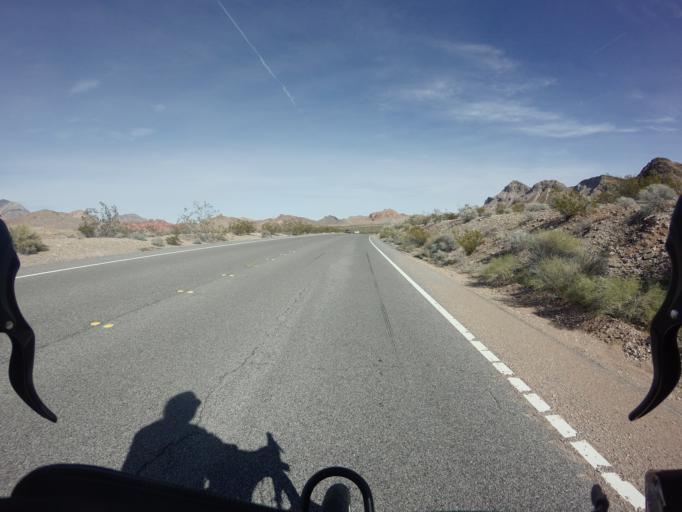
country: US
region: Nevada
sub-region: Clark County
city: Boulder City
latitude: 36.2101
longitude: -114.6574
